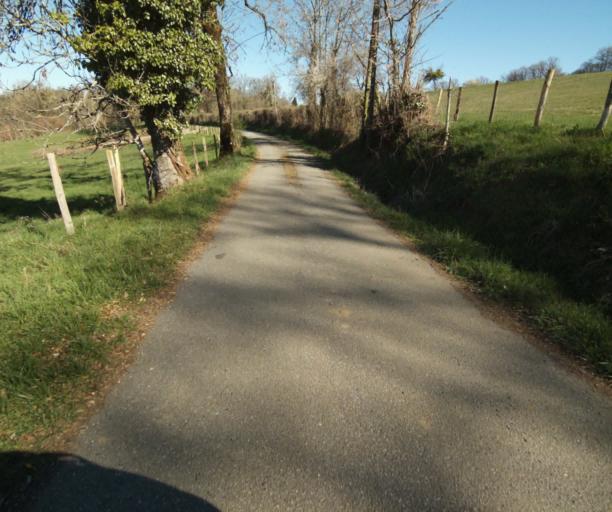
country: FR
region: Limousin
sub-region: Departement de la Correze
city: Chamboulive
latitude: 45.4015
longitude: 1.6990
